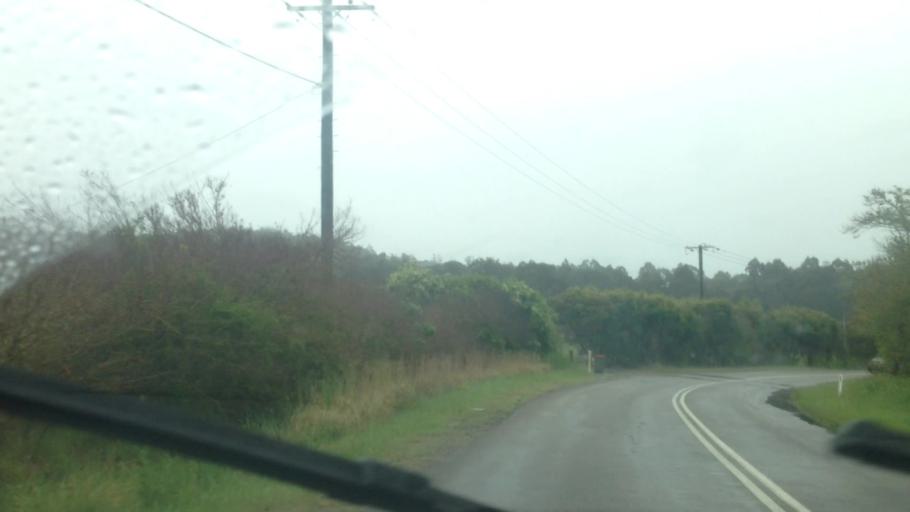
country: AU
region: New South Wales
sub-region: Wyong Shire
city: Little Jilliby
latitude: -33.2171
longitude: 151.3713
